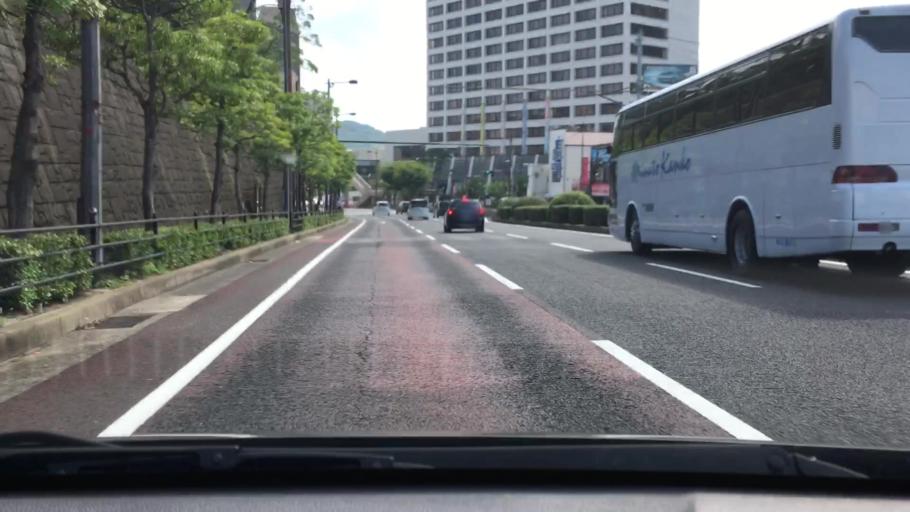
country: JP
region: Nagasaki
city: Sasebo
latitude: 33.1814
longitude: 129.7164
